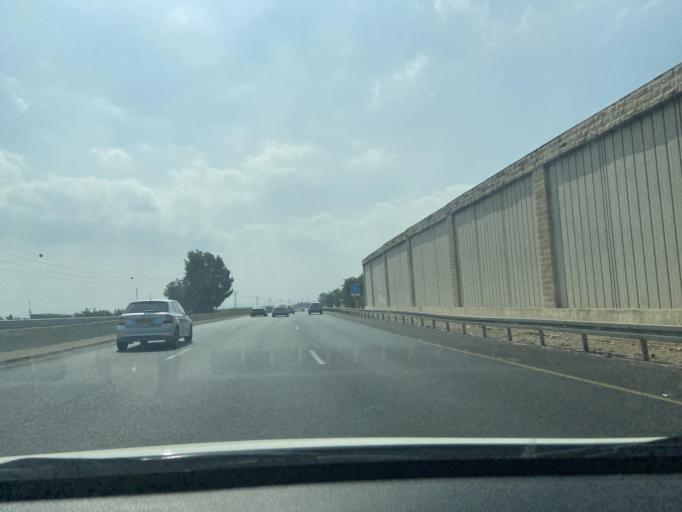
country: IL
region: Northern District
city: `Akko
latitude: 32.9441
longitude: 35.0955
